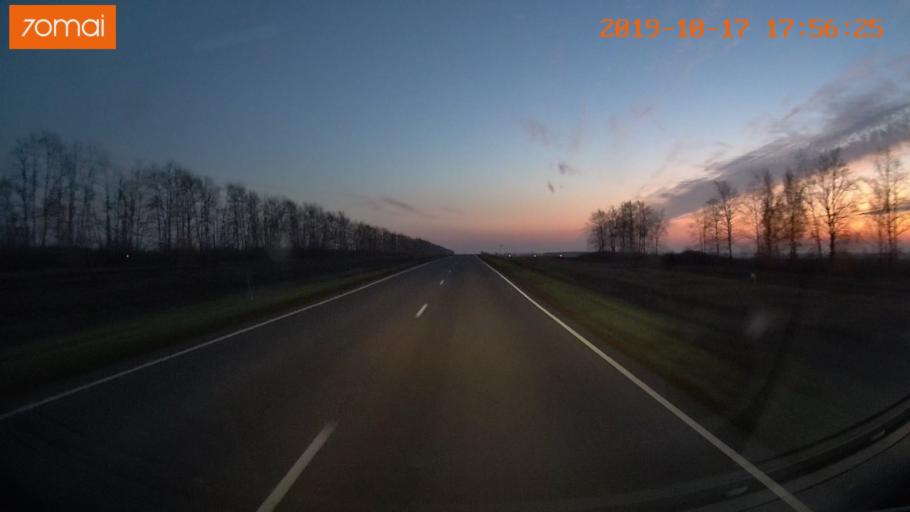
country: RU
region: Tula
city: Kurkino
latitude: 53.5795
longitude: 38.6469
